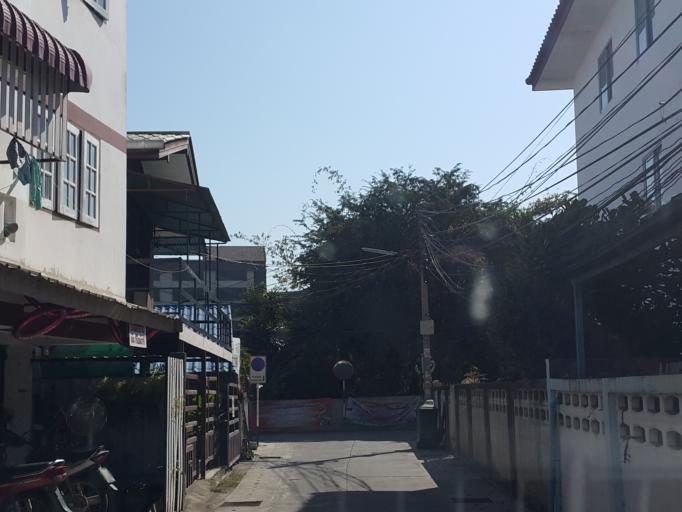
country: TH
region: Chiang Mai
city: Chiang Mai
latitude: 18.8072
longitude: 98.9692
